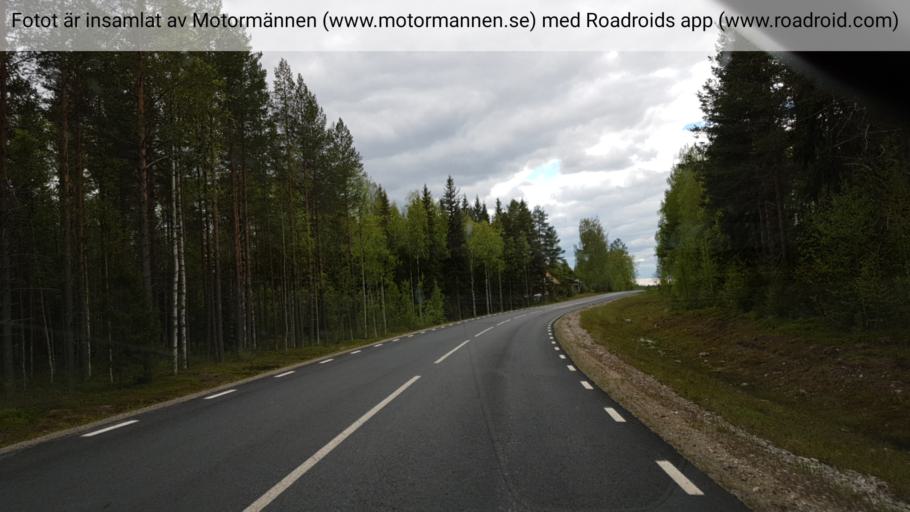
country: SE
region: Vaesterbotten
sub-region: Skelleftea Kommun
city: Langsele
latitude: 64.5622
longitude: 19.9304
